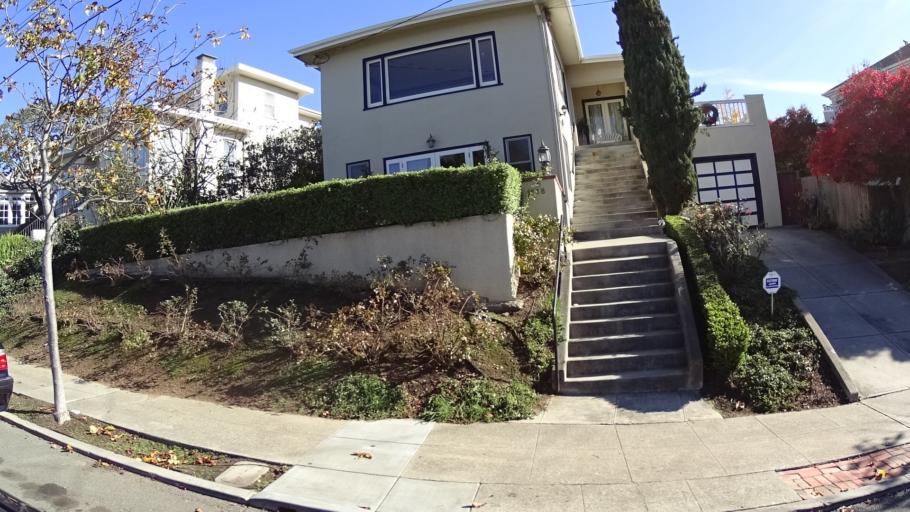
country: US
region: California
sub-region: Alameda County
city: Piedmont
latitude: 37.8192
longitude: -122.2375
